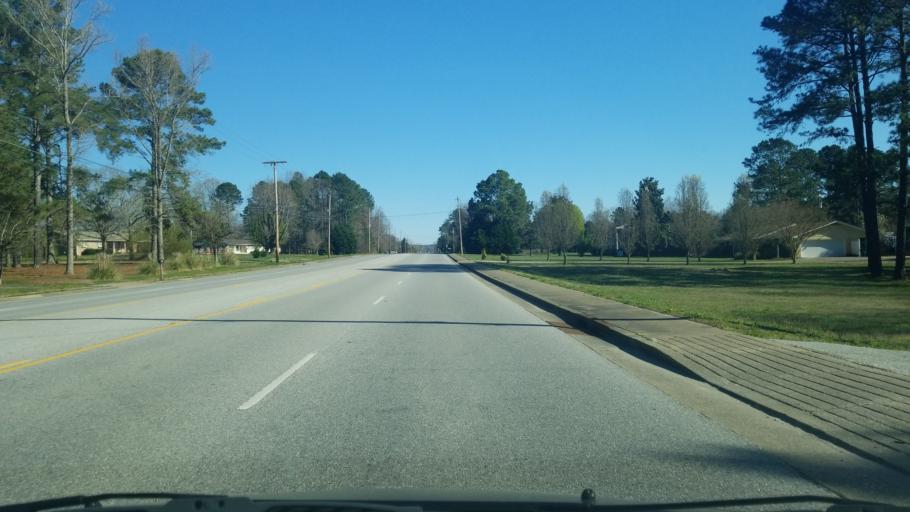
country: US
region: Tennessee
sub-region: Hamilton County
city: Middle Valley
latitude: 35.1782
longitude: -85.1709
